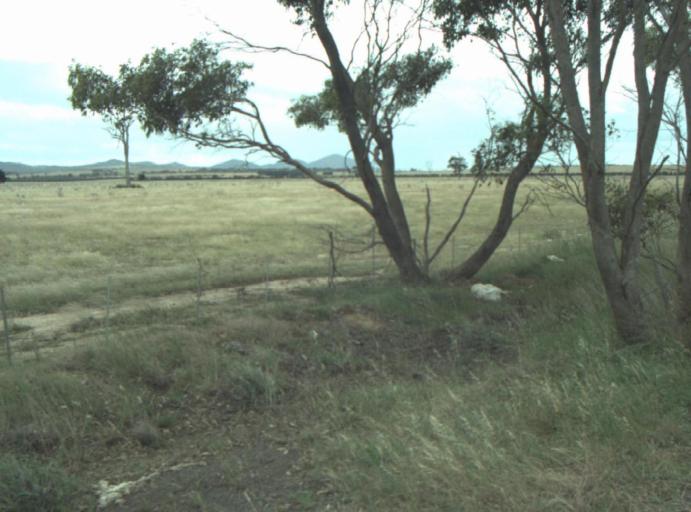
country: AU
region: Victoria
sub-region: Greater Geelong
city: Lara
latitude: -37.8725
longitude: 144.3501
